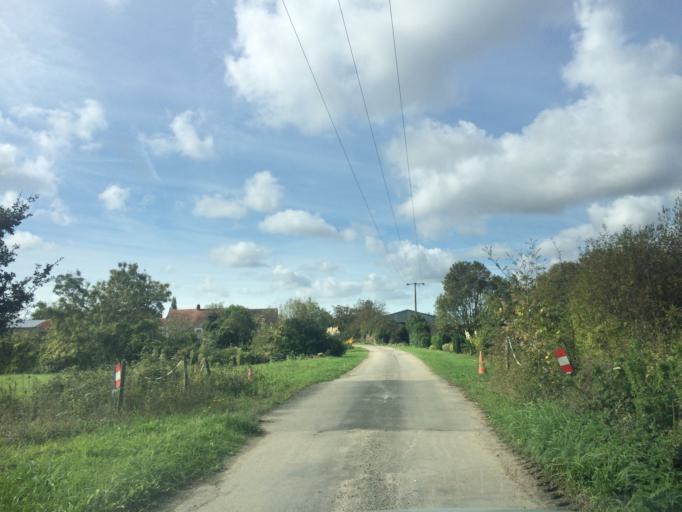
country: FR
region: Pays de la Loire
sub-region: Departement de la Loire-Atlantique
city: Chemere
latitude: 47.1401
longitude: -1.9093
